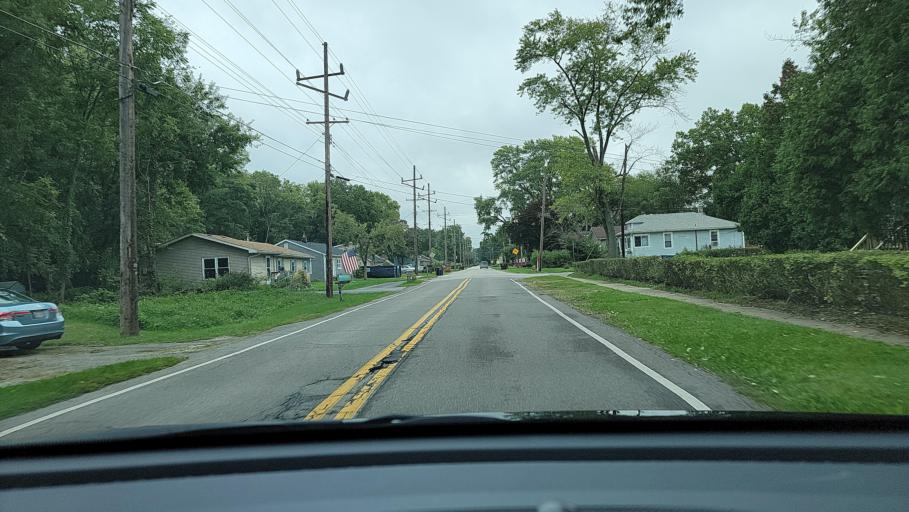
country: US
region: Indiana
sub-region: Porter County
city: Portage
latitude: 41.5717
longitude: -87.1934
